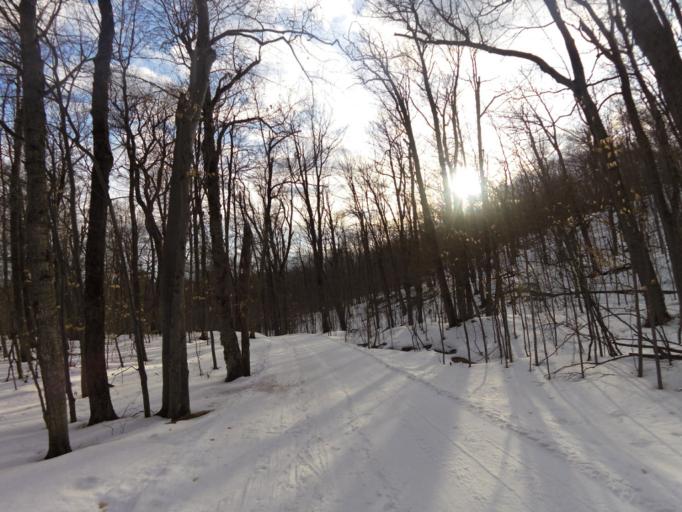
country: CA
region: Quebec
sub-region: Outaouais
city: Gatineau
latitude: 45.4964
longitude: -75.8464
